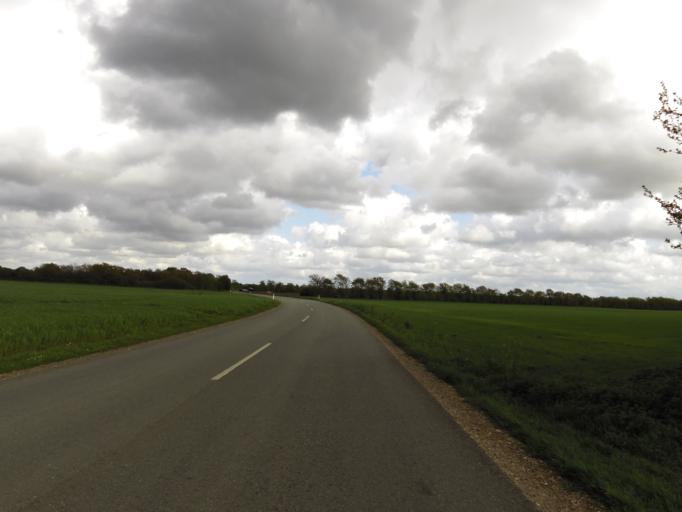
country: DK
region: South Denmark
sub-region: Haderslev Kommune
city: Gram
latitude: 55.3049
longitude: 9.0053
